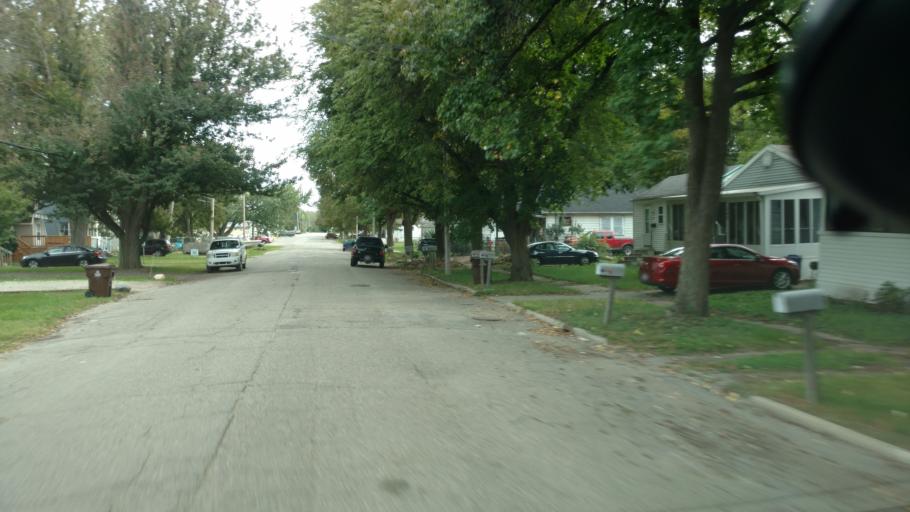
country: US
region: Michigan
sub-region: Ingham County
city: East Lansing
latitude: 42.7322
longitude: -84.5152
